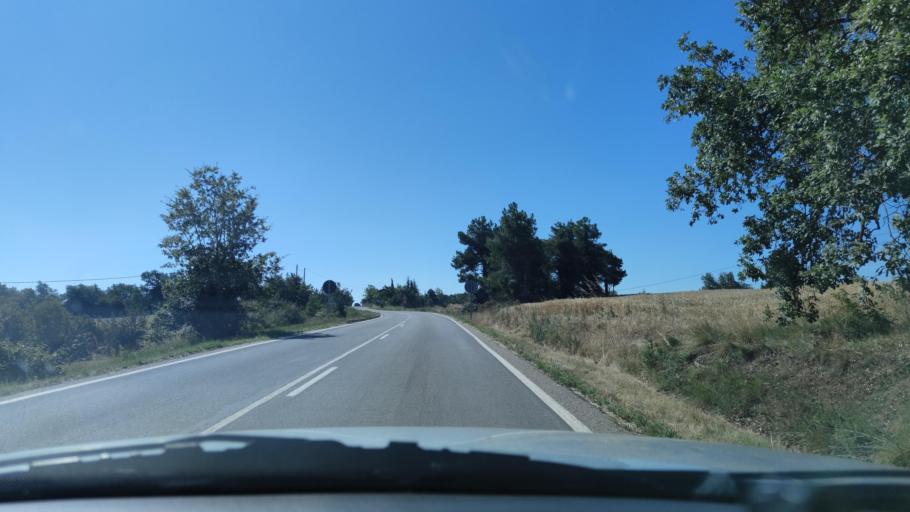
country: ES
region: Catalonia
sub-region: Provincia de Lleida
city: Solsona
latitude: 41.9178
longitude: 1.5019
